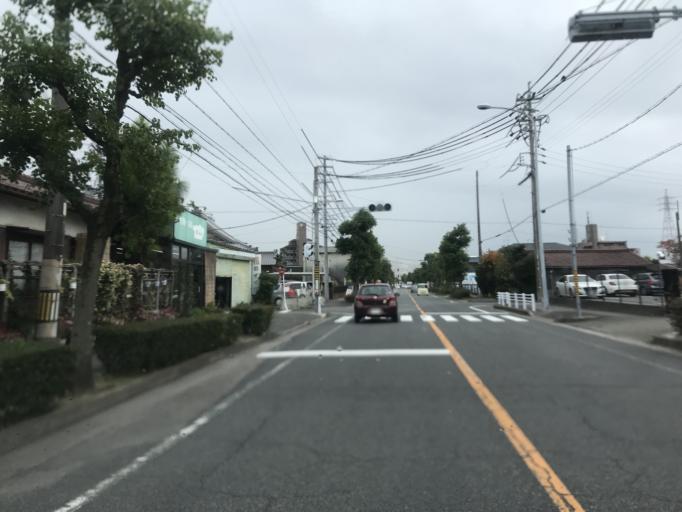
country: JP
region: Aichi
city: Nagoya-shi
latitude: 35.2044
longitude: 136.8397
